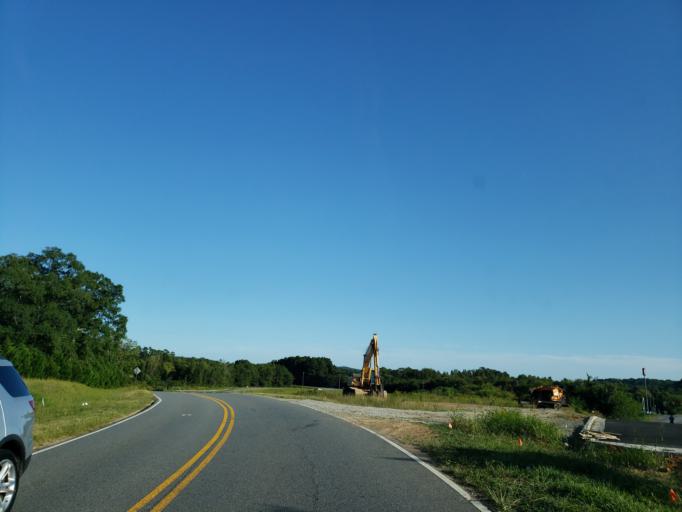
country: US
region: Georgia
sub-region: Bartow County
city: Rydal
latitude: 34.2761
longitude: -84.8064
